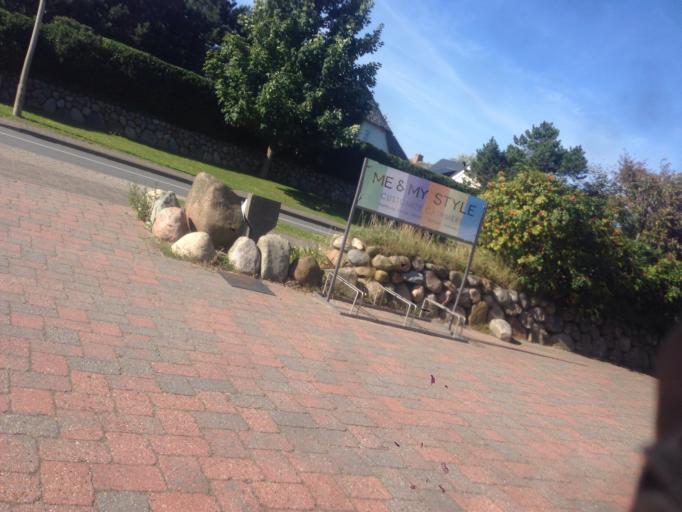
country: DE
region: Schleswig-Holstein
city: Tinnum
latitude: 54.9530
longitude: 8.3420
